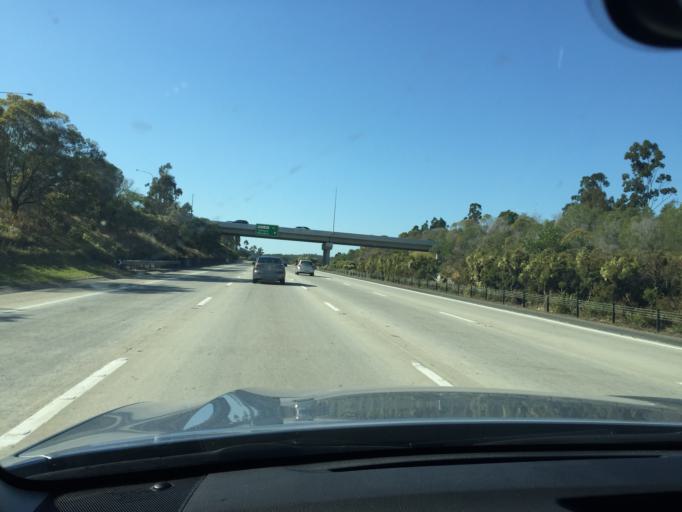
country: AU
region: Queensland
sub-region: Gold Coast
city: Ormeau Hills
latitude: -27.7852
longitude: 153.2557
